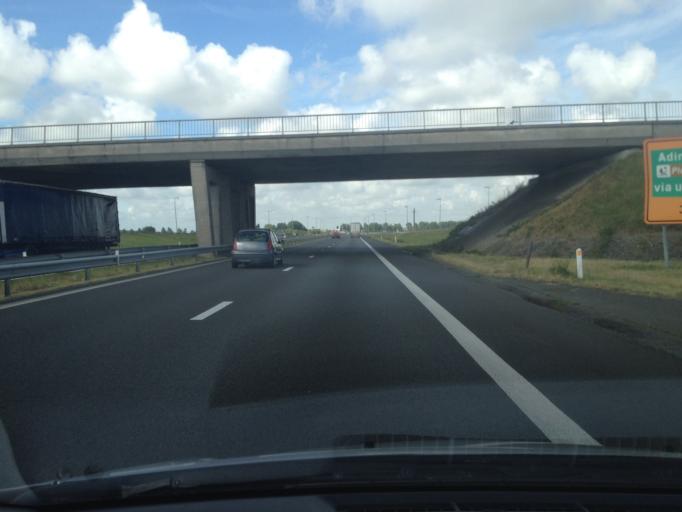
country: BE
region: Flanders
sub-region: Provincie West-Vlaanderen
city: Veurne
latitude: 51.0806
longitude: 2.7133
